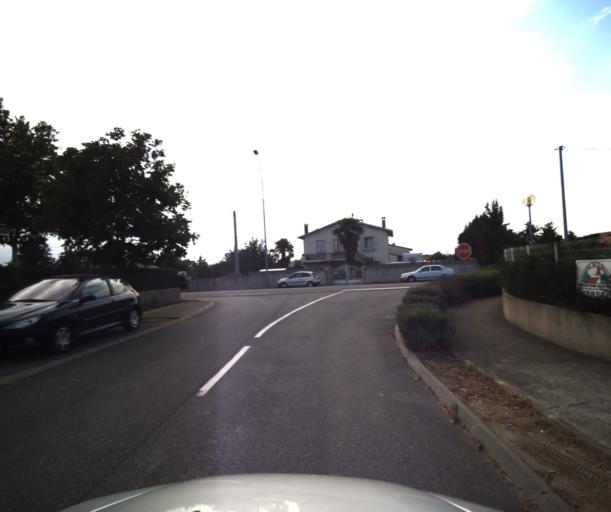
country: FR
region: Midi-Pyrenees
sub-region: Departement de la Haute-Garonne
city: Muret
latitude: 43.4435
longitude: 1.3157
